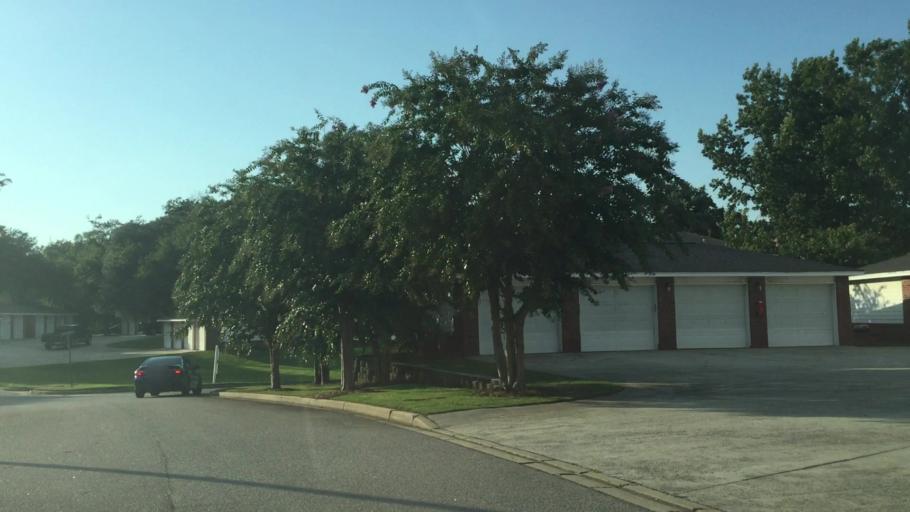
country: US
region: South Carolina
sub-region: Sumter County
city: Lakewood
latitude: 33.8730
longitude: -80.3541
